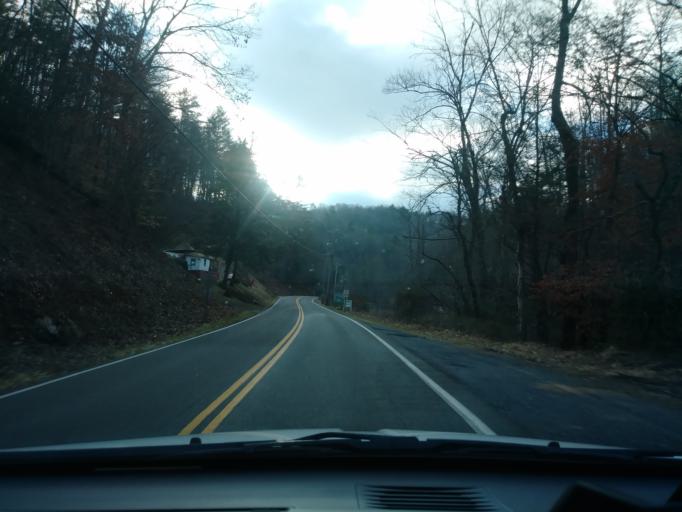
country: US
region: Tennessee
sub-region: Carter County
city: Pine Crest
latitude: 36.2158
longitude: -82.2153
